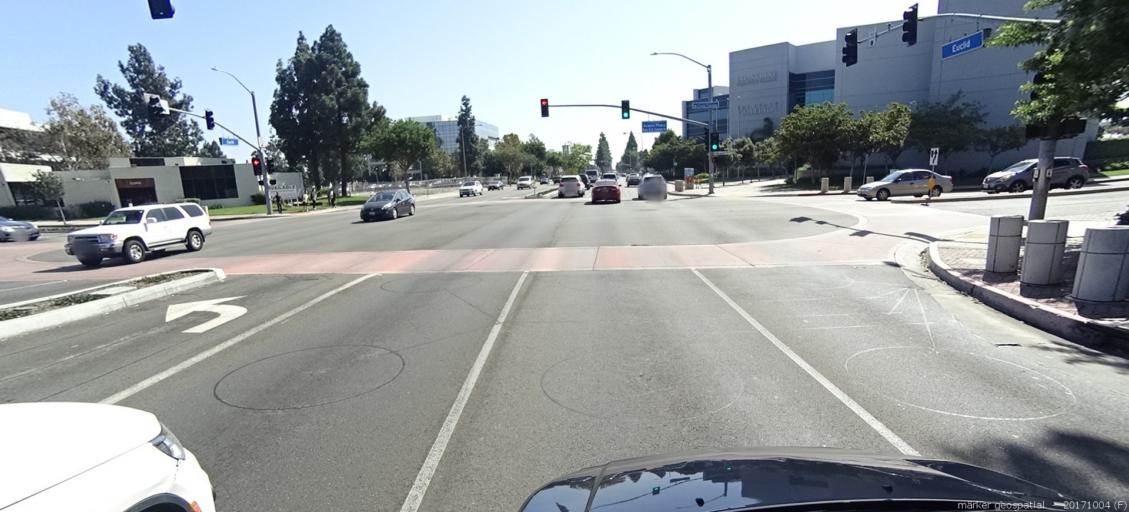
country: US
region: California
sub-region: Orange County
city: Garden Grove
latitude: 33.7764
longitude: -117.9382
